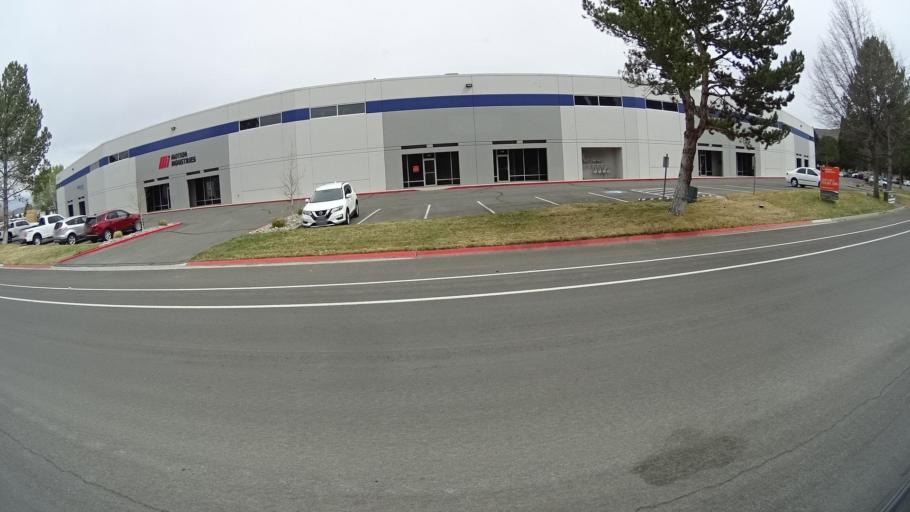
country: US
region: Nevada
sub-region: Washoe County
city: Sparks
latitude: 39.5133
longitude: -119.7331
